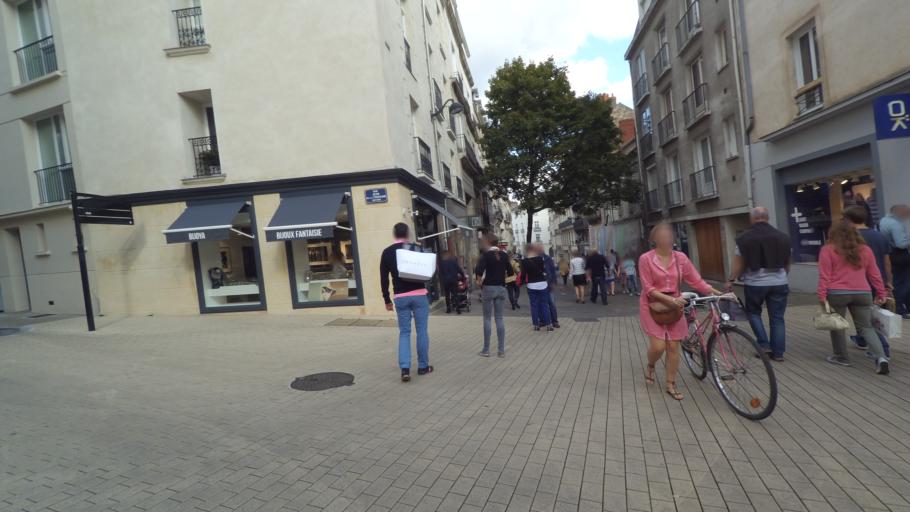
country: FR
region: Pays de la Loire
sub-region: Departement de la Loire-Atlantique
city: Nantes
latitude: 47.2140
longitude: -1.5619
